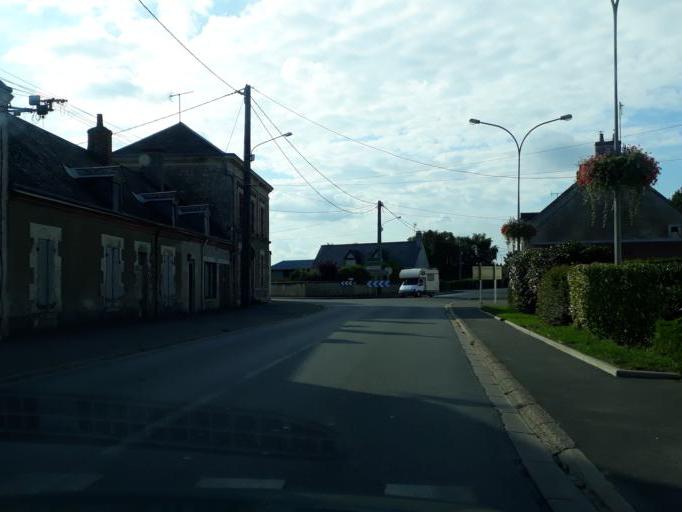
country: FR
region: Centre
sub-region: Departement du Loir-et-Cher
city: Ouzouer-le-Marche
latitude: 47.9038
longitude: 1.4610
